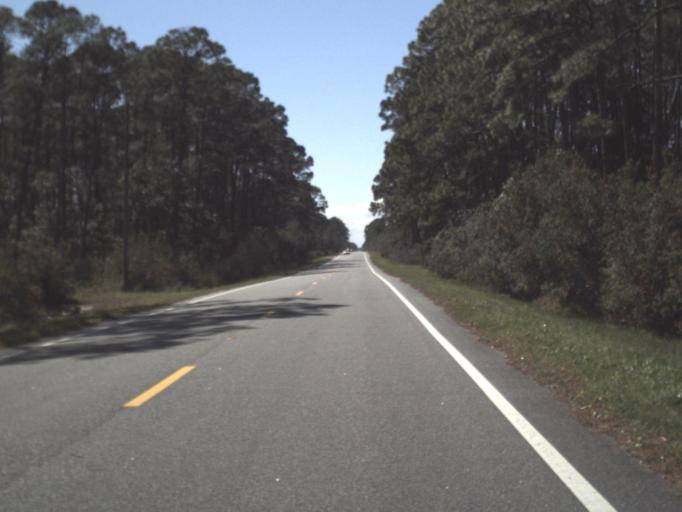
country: US
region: Florida
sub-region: Franklin County
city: Carrabelle
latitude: 29.9270
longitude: -84.4702
